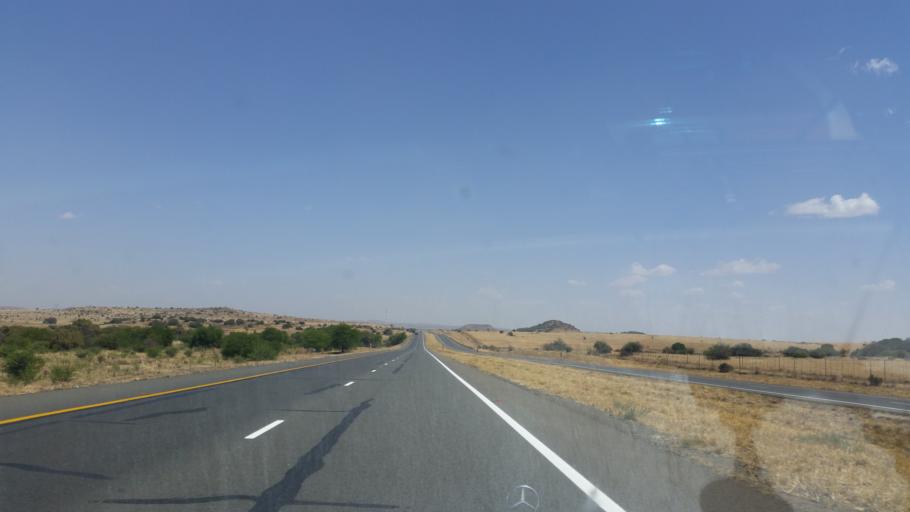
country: ZA
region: Orange Free State
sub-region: Lejweleputswa District Municipality
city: Brandfort
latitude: -28.9210
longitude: 26.4407
